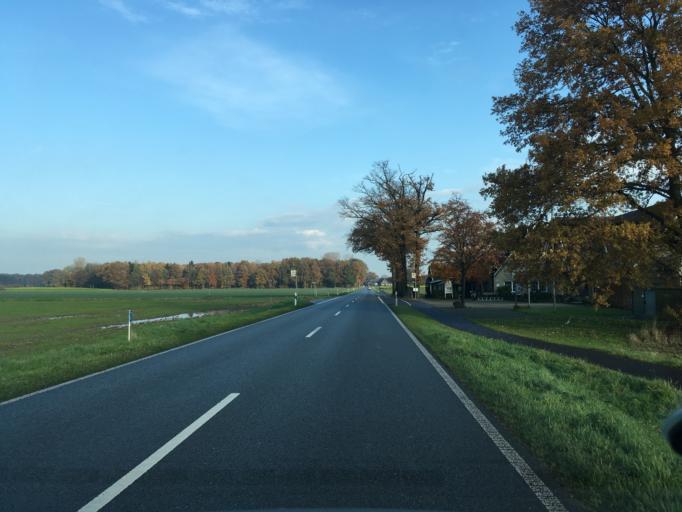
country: DE
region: North Rhine-Westphalia
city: Stadtlohn
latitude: 52.0046
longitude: 6.9376
